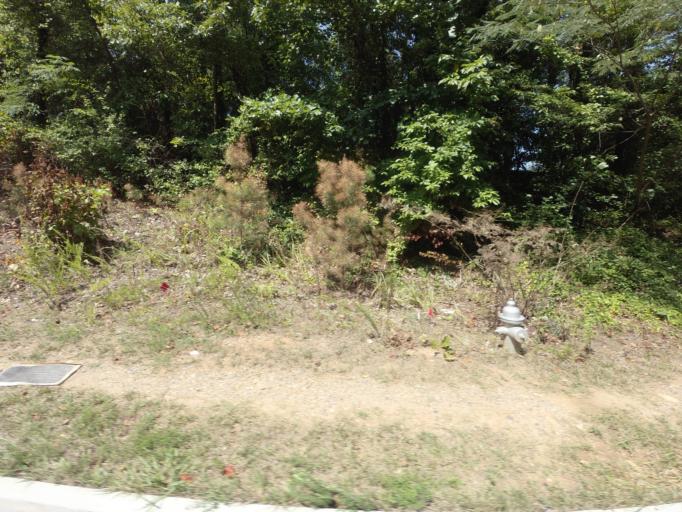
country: US
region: Georgia
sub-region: Fulton County
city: Alpharetta
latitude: 34.0054
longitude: -84.2769
